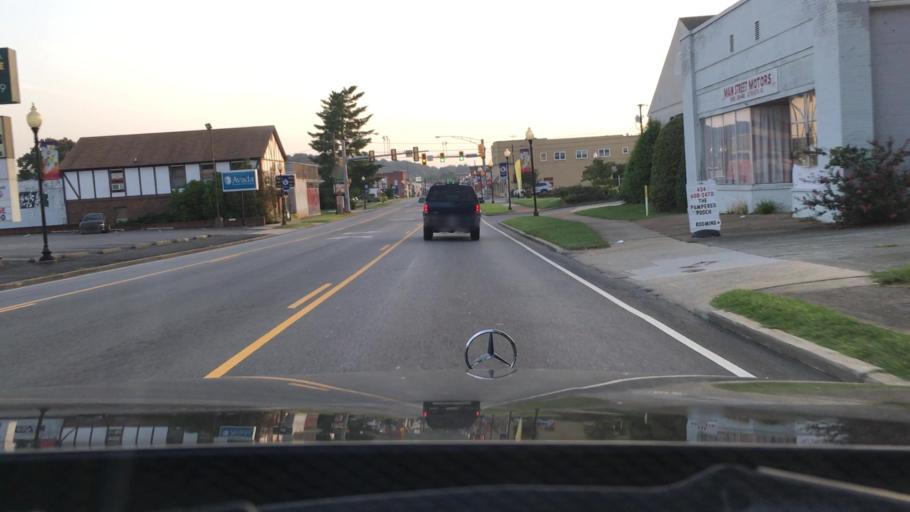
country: US
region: Virginia
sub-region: Campbell County
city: Altavista
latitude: 37.1144
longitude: -79.2820
